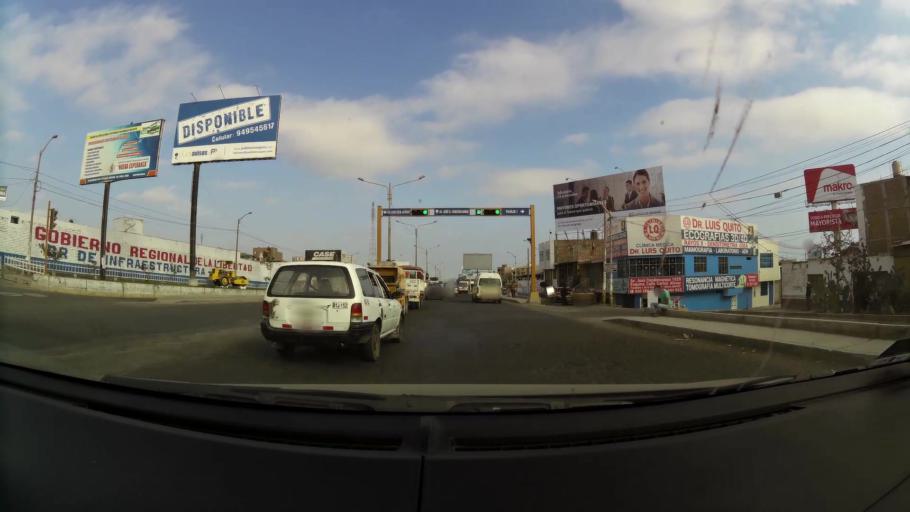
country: PE
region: La Libertad
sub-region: Provincia de Trujillo
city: La Esperanza
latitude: -8.0842
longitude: -79.0440
